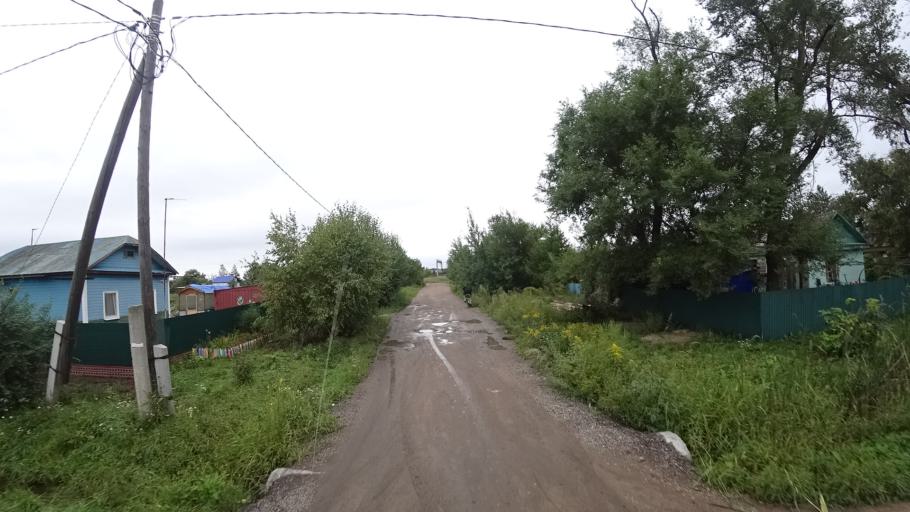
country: RU
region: Primorskiy
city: Chernigovka
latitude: 44.3438
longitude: 132.5338
